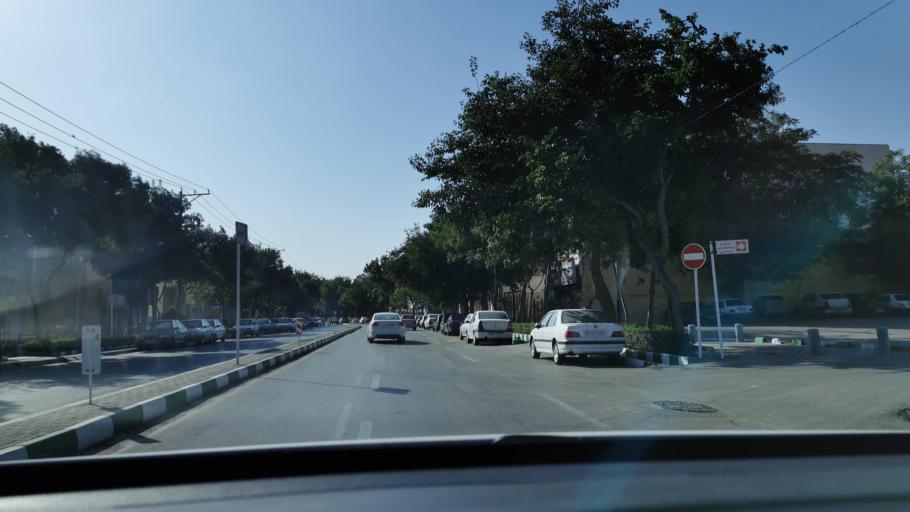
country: IR
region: Razavi Khorasan
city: Mashhad
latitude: 36.2983
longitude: 59.6200
